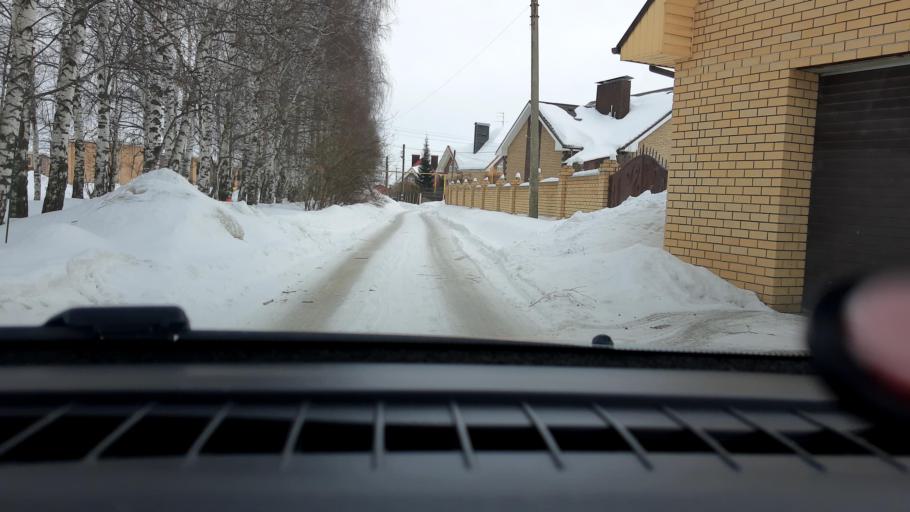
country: RU
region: Nizjnij Novgorod
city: Afonino
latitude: 56.1979
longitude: 44.1149
